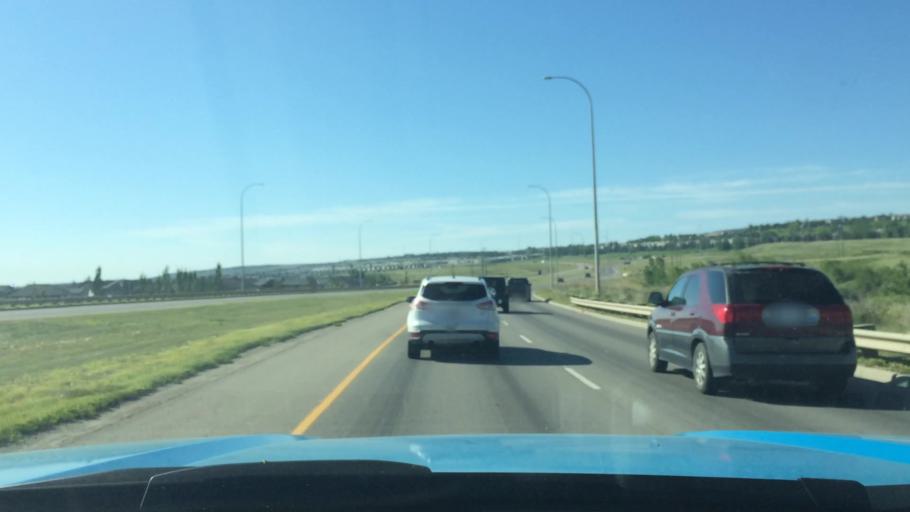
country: CA
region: Alberta
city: Calgary
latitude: 51.1614
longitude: -114.1422
